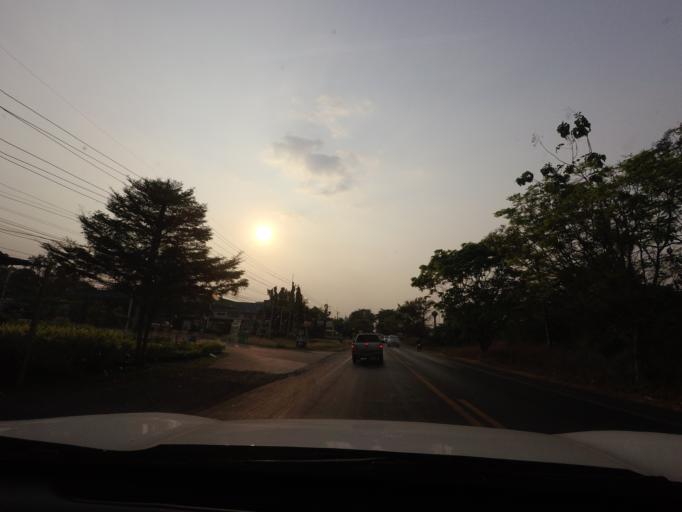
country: TH
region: Nakhon Nayok
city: Pak Phli
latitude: 14.1506
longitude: 101.3257
